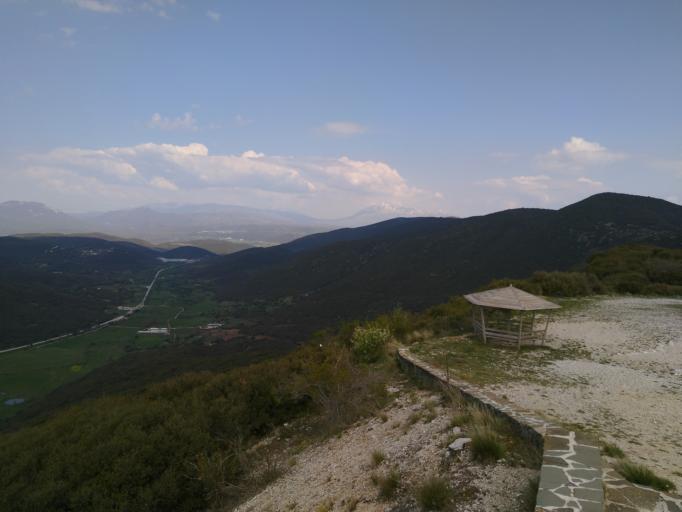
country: GR
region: Epirus
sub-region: Nomos Ioanninon
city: Asprangeloi
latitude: 39.8380
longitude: 20.7030
